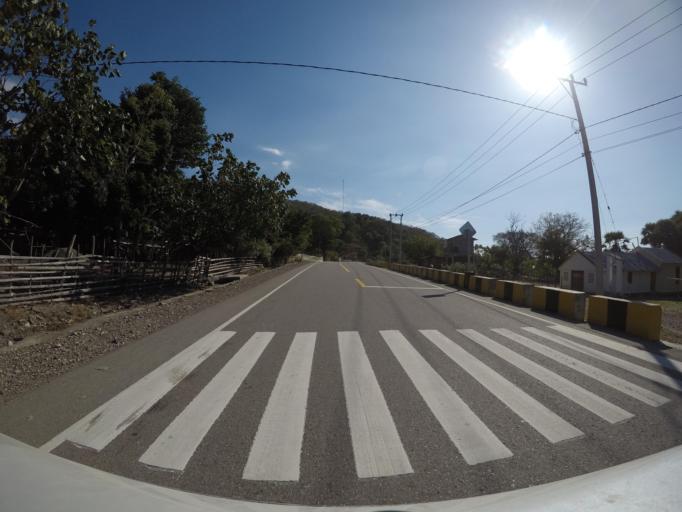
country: TL
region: Liquica
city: Maubara
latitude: -8.6376
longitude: 125.1379
